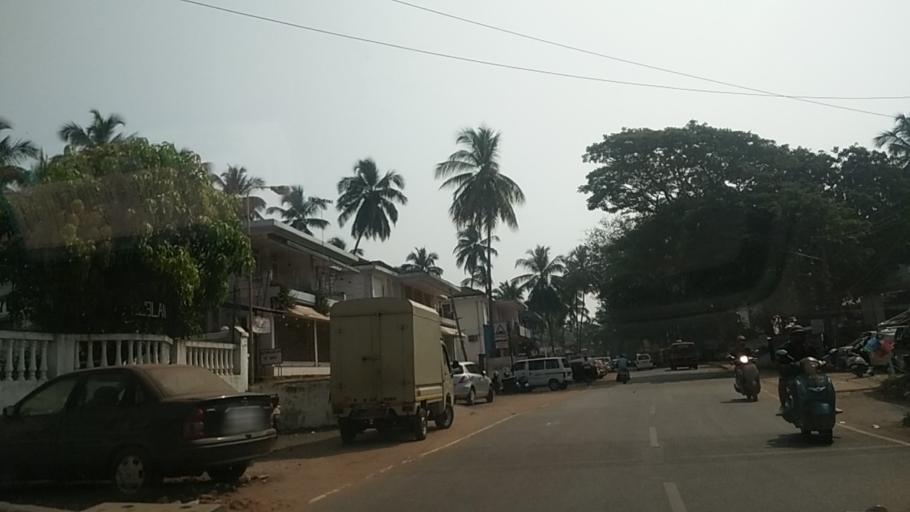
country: IN
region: Goa
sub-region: North Goa
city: Candolim
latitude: 15.5159
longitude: 73.7684
